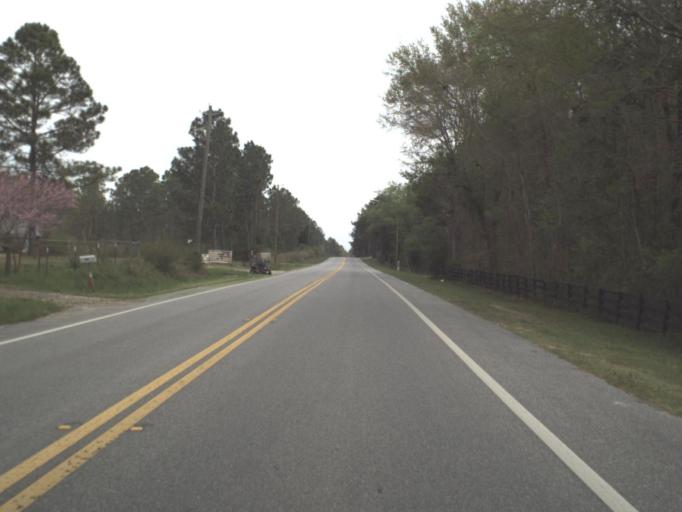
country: US
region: Florida
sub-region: Holmes County
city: Bonifay
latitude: 30.8350
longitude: -85.6668
